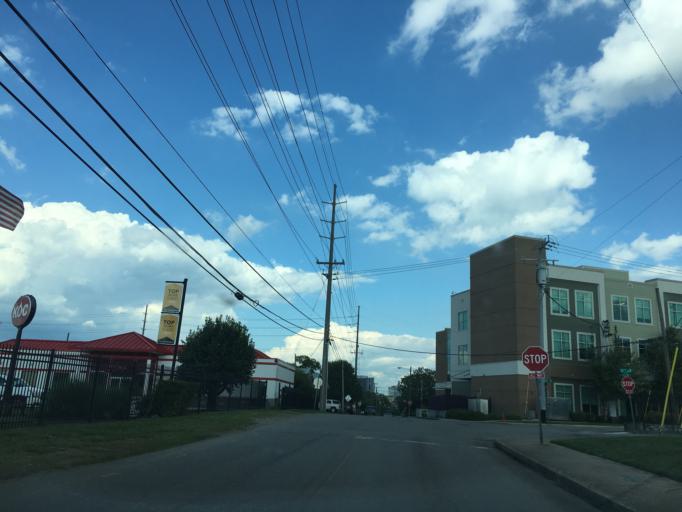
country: US
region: Tennessee
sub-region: Davidson County
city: Nashville
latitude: 36.1578
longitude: -86.8082
